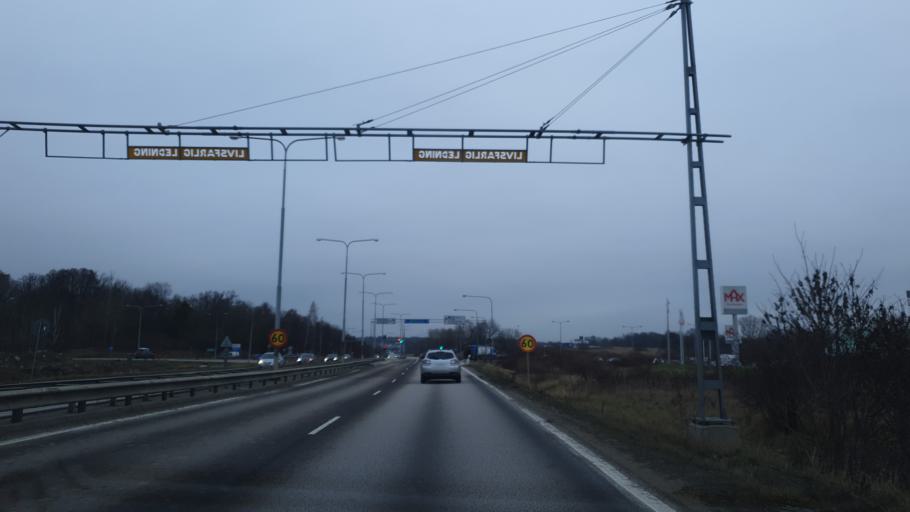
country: SE
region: Blekinge
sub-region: Karlskrona Kommun
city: Karlskrona
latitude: 56.1951
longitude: 15.6305
